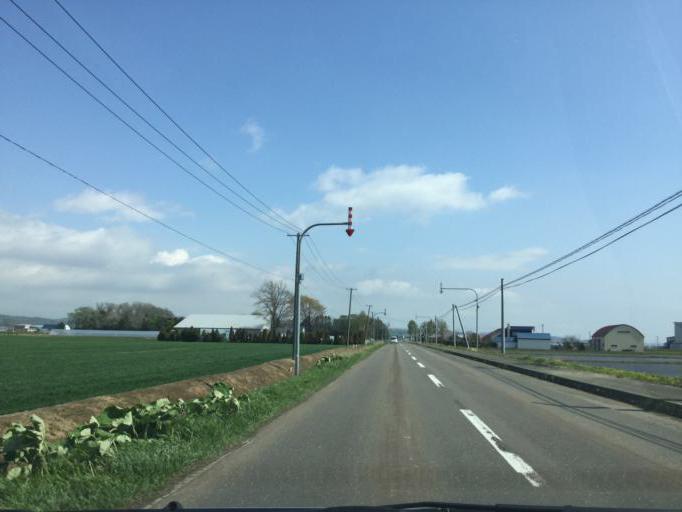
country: JP
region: Hokkaido
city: Iwamizawa
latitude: 43.1423
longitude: 141.7241
